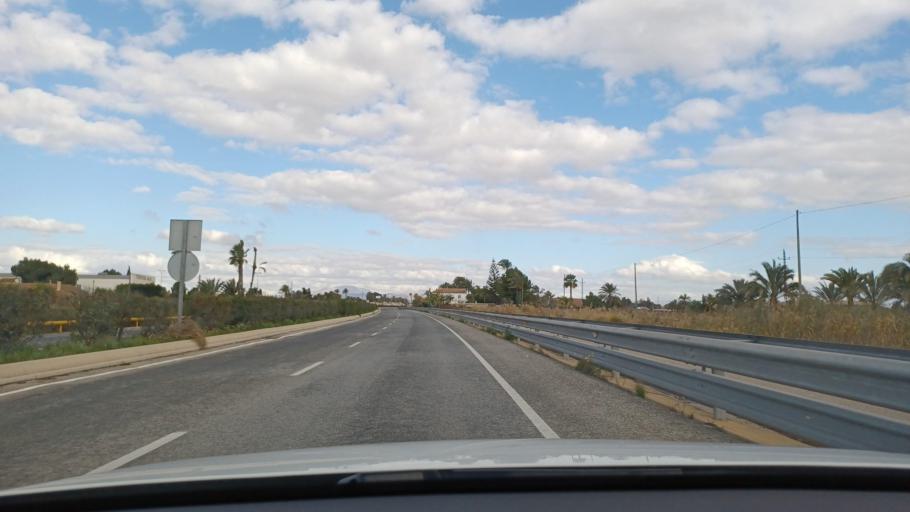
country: ES
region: Valencia
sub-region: Provincia de Alicante
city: Elche
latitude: 38.1894
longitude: -0.7010
